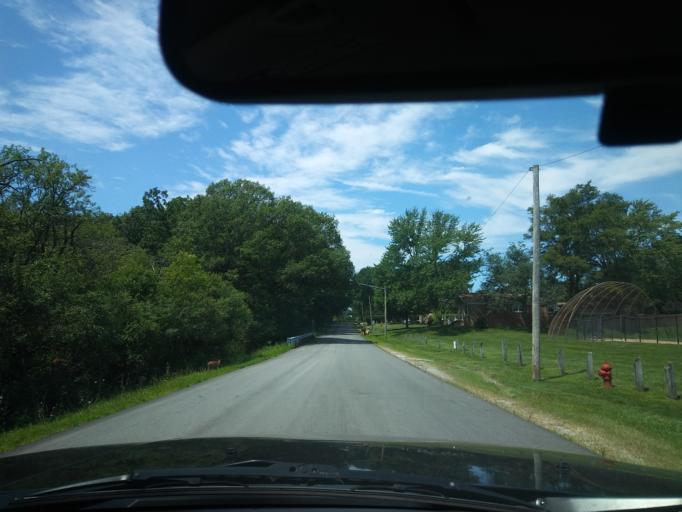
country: US
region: Illinois
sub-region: Cook County
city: Oak Forest
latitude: 41.5957
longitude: -87.7516
